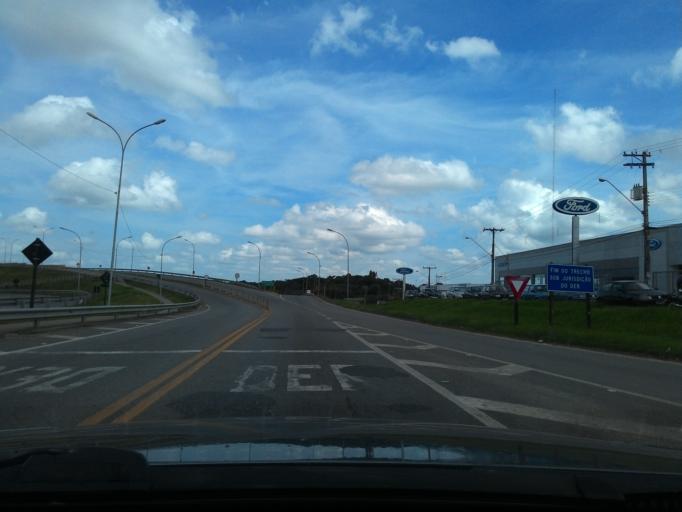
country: BR
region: Sao Paulo
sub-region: Registro
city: Registro
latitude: -24.5073
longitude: -47.8511
